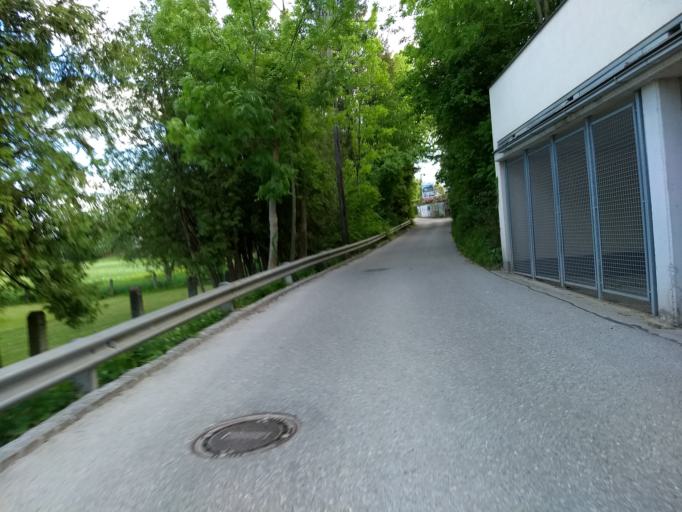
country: AT
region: Salzburg
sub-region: Politischer Bezirk Salzburg-Umgebung
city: Bergheim
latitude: 47.8189
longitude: 13.0129
